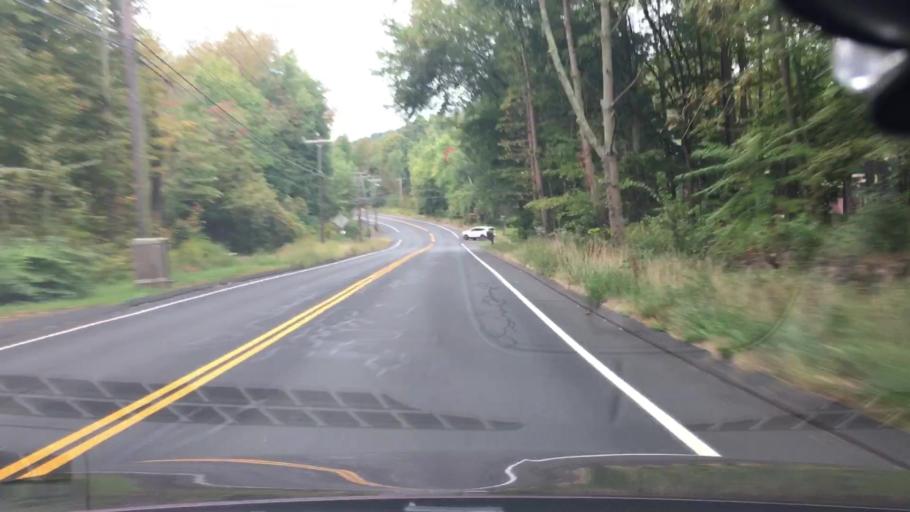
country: US
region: Connecticut
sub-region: Tolland County
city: Somers
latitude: 41.9814
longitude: -72.4098
